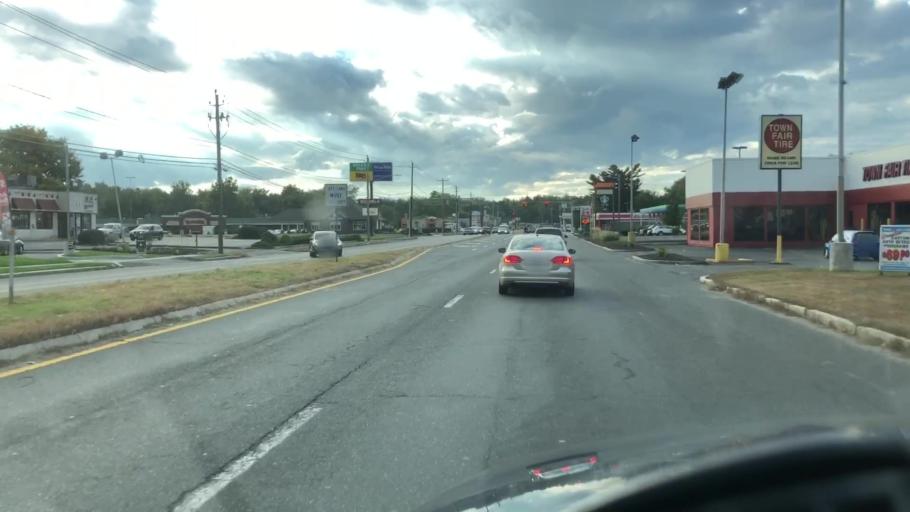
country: US
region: Massachusetts
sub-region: Hampden County
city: Westfield
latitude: 42.1141
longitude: -72.7265
